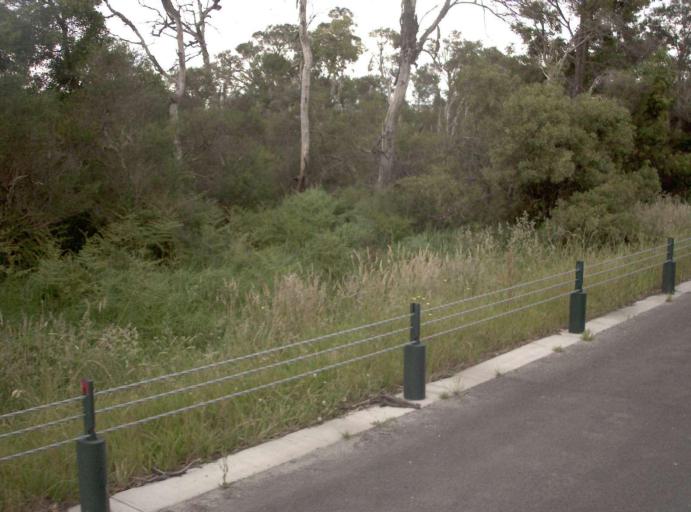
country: AU
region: Victoria
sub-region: Casey
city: Tooradin
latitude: -38.2167
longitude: 145.4022
